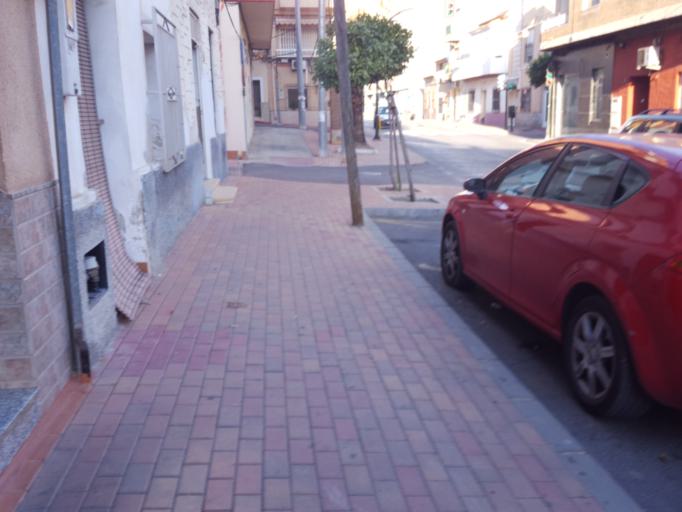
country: ES
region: Murcia
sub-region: Murcia
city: Murcia
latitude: 38.0006
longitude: -1.1709
